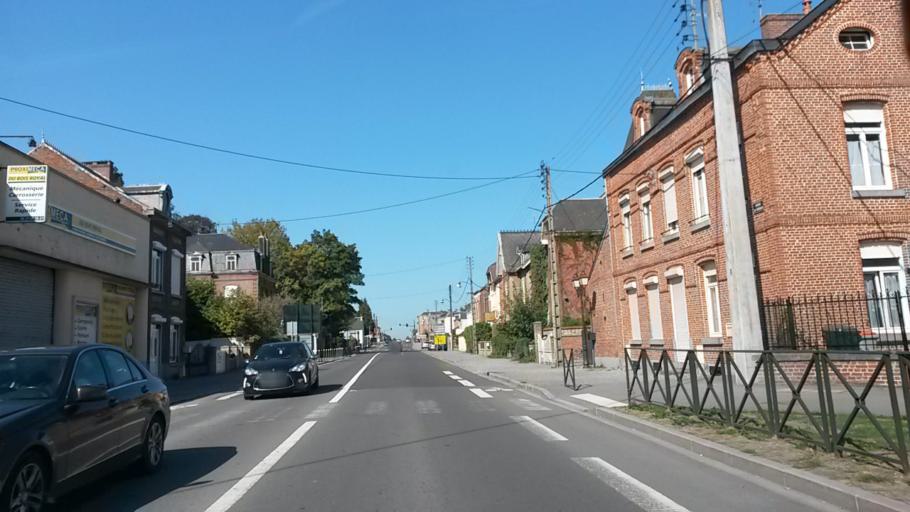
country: FR
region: Nord-Pas-de-Calais
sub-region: Departement du Nord
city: Avesnes-sur-Helpe
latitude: 50.1190
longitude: 3.9304
